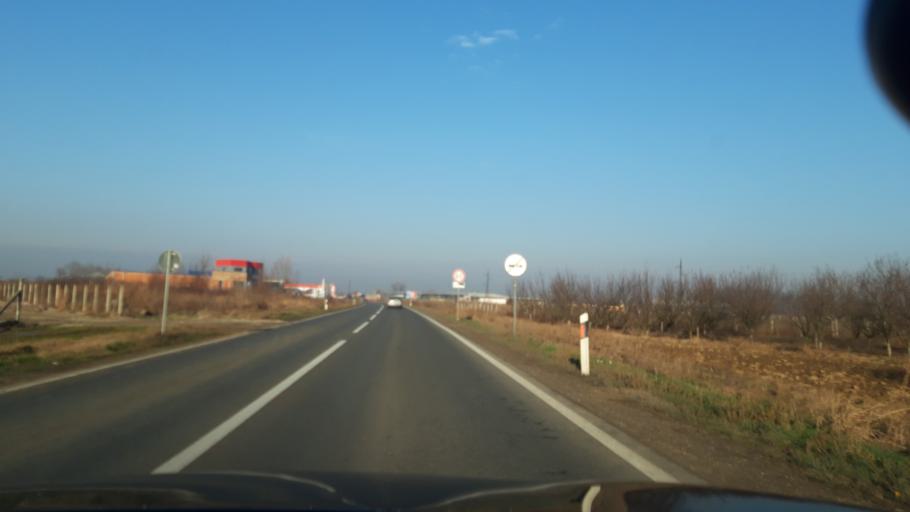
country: RS
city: Majur
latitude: 44.7605
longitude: 19.6434
